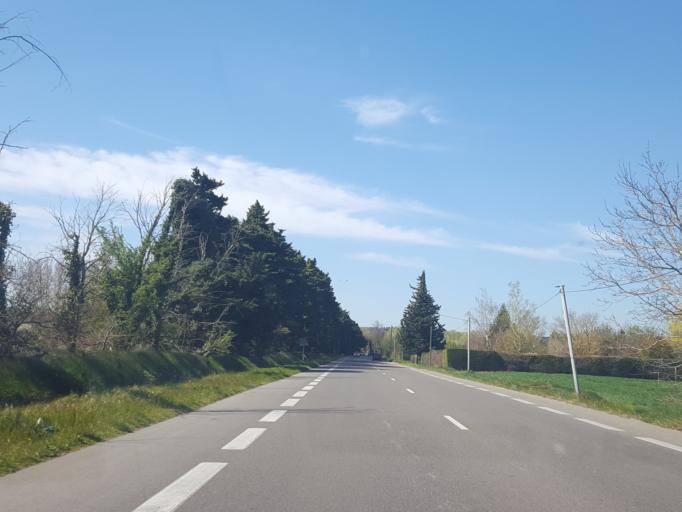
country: FR
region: Provence-Alpes-Cote d'Azur
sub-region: Departement du Vaucluse
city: Jonquerettes
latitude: 43.9637
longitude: 4.9568
